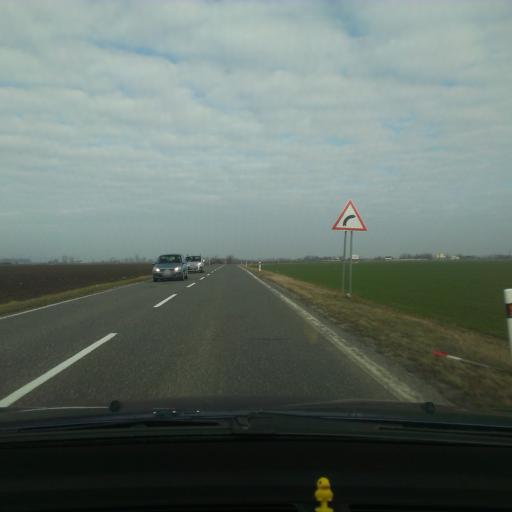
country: SK
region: Trnavsky
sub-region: Okres Trnava
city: Piestany
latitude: 48.5324
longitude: 17.7969
